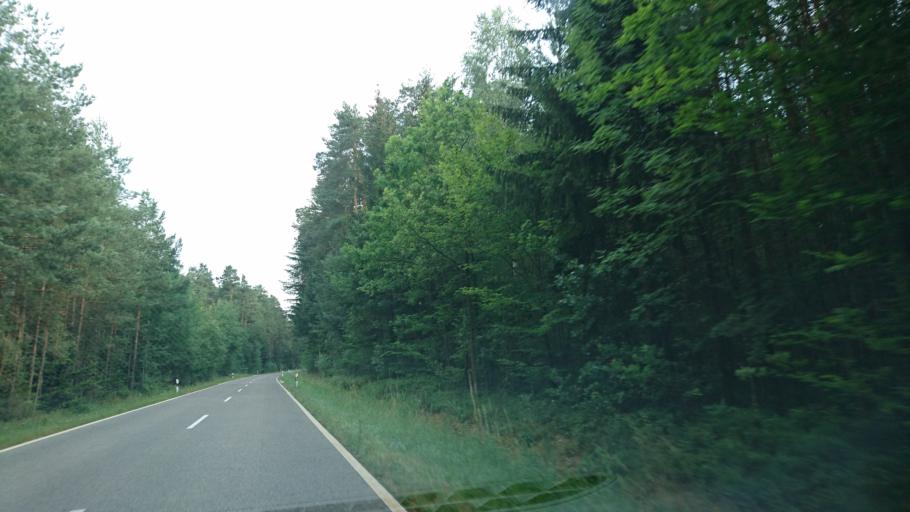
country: DE
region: Bavaria
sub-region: Regierungsbezirk Mittelfranken
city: Heideck
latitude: 49.1698
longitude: 11.1191
